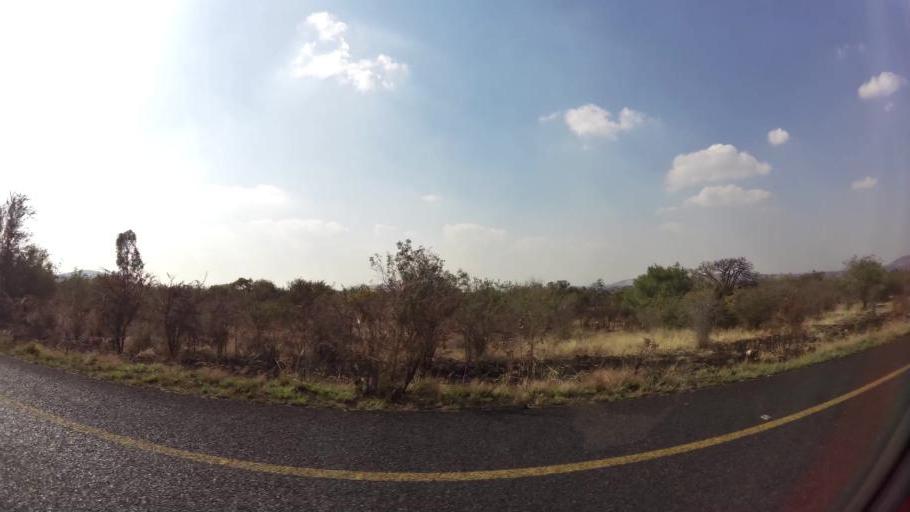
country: ZA
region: North-West
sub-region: Bojanala Platinum District Municipality
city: Rustenburg
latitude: -25.6039
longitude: 27.1385
